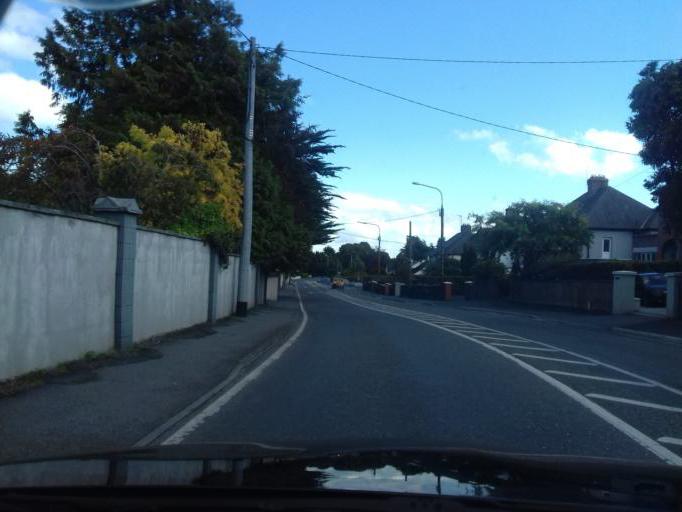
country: IE
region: Leinster
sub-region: Uibh Fhaili
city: Tullamore
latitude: 53.2688
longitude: -7.4898
